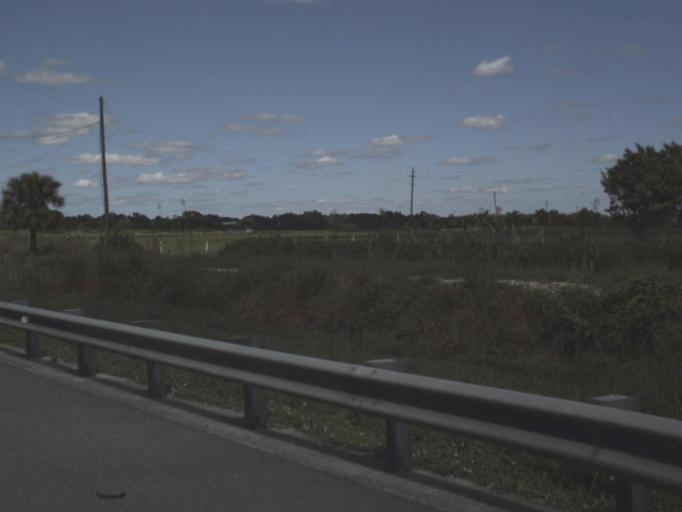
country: US
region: Florida
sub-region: Collier County
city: Lely Resort
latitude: 26.0306
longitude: -81.6479
